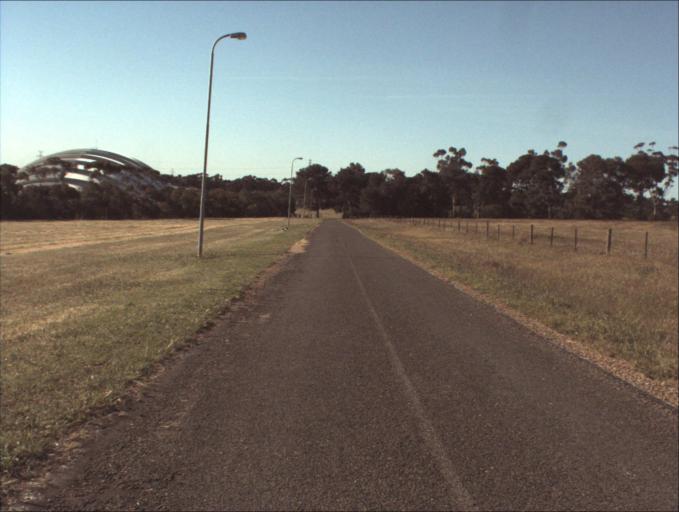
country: AU
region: South Australia
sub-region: Port Adelaide Enfield
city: Enfield
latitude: -34.8452
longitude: 138.6138
